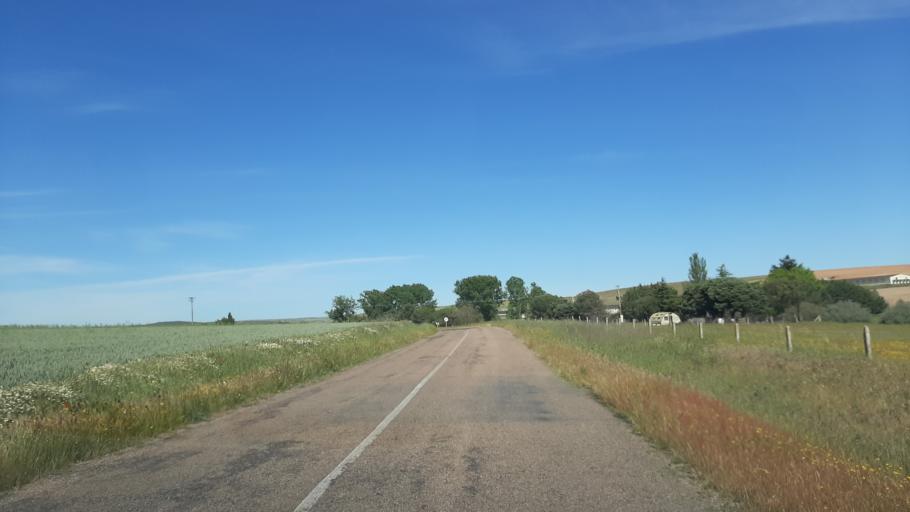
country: ES
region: Castille and Leon
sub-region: Provincia de Salamanca
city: Aldeaseca de Alba
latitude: 40.8209
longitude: -5.4771
